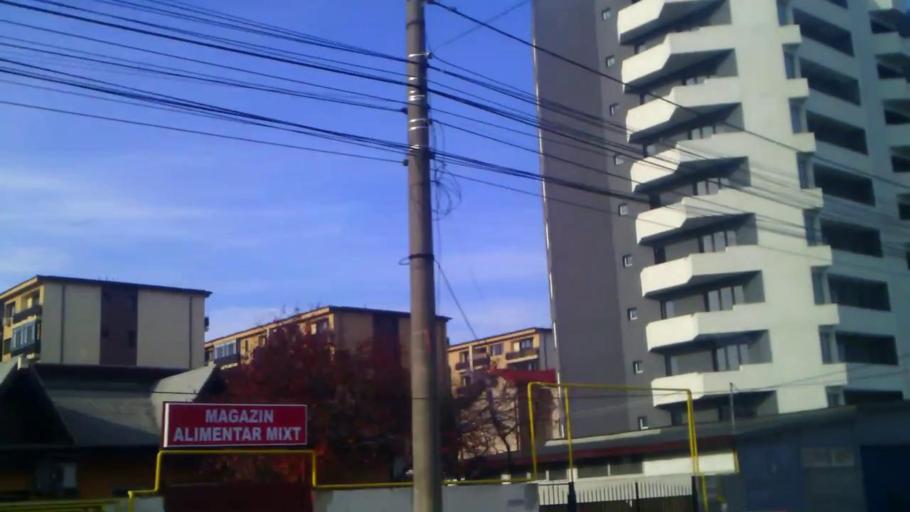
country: RO
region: Ilfov
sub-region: Comuna Popesti-Leordeni
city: Popesti-Leordeni
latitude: 44.3681
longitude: 26.1435
